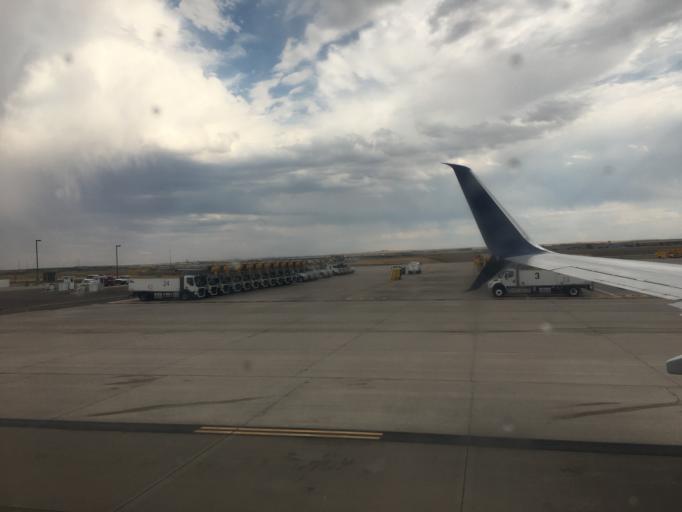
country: US
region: Colorado
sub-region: Weld County
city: Lochbuie
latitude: 39.8519
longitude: -104.6872
